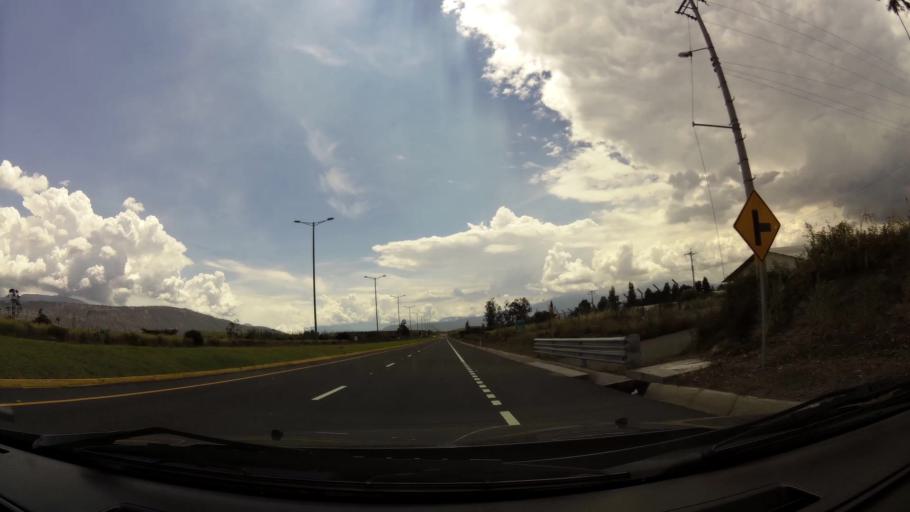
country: EC
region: Pichincha
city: Quito
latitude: -0.1222
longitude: -78.3651
